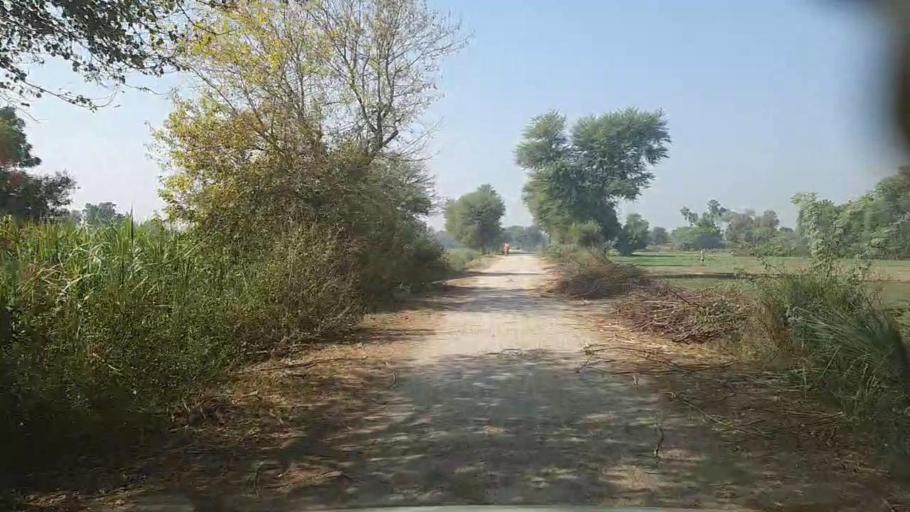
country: PK
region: Sindh
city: Kandiari
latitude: 26.9942
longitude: 68.4844
